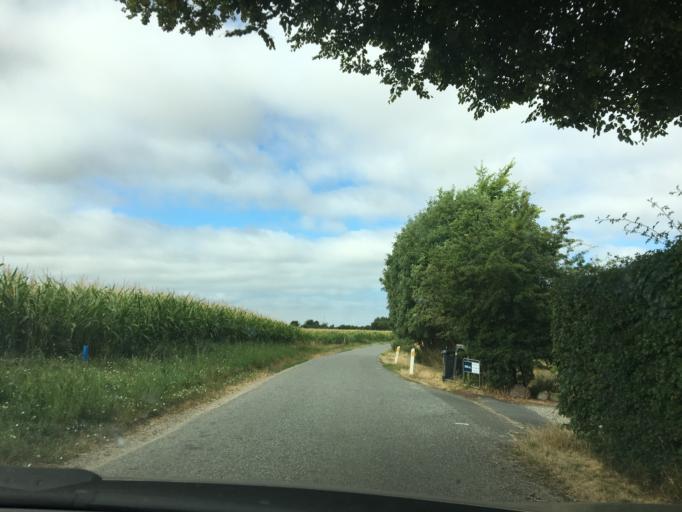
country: DK
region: South Denmark
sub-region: Middelfart Kommune
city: Norre Aby
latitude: 55.5017
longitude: 9.8459
